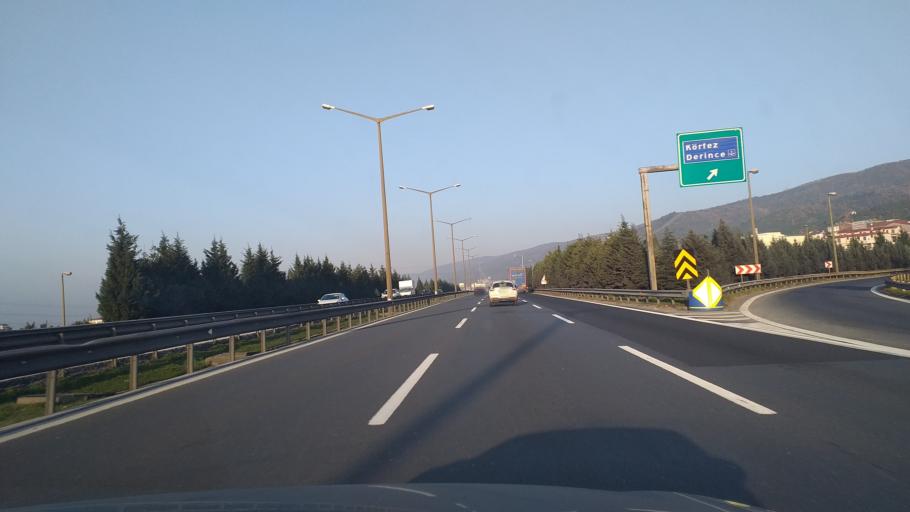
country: TR
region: Kocaeli
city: Korfez
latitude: 40.7718
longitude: 29.7730
